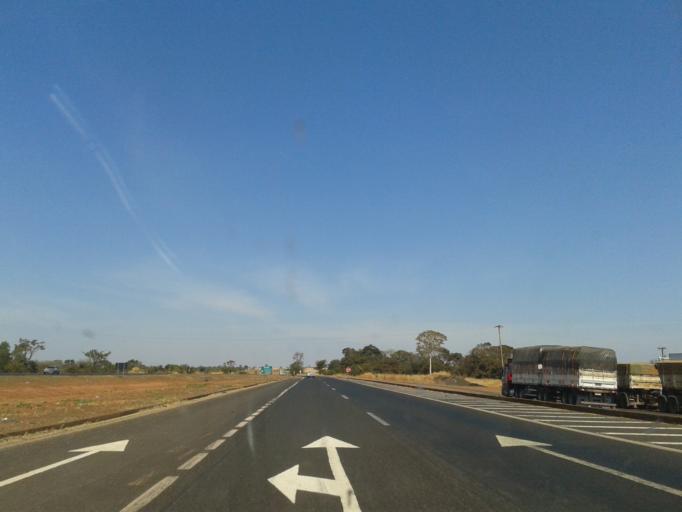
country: BR
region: Minas Gerais
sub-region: Monte Alegre De Minas
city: Monte Alegre de Minas
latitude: -18.8170
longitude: -49.0875
